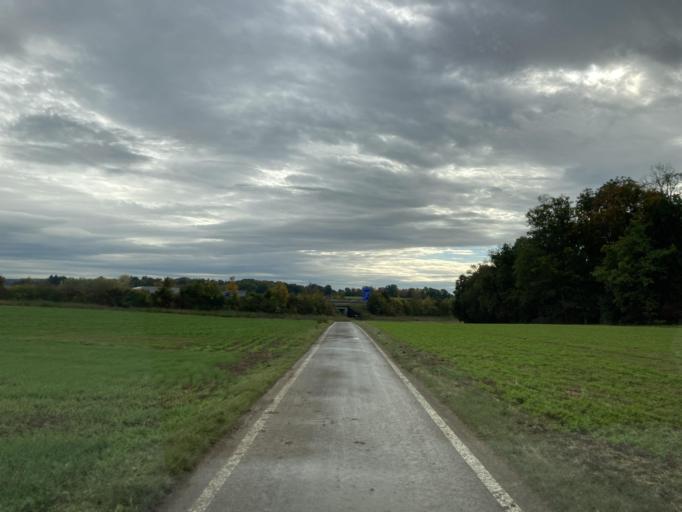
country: DE
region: Baden-Wuerttemberg
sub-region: Regierungsbezirk Stuttgart
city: Bondorf
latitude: 48.5120
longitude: 8.8543
